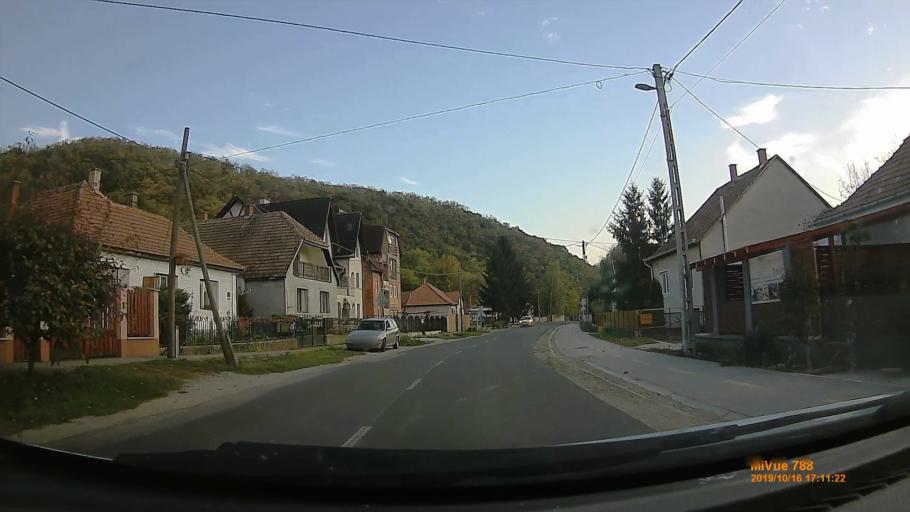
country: HU
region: Heves
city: Egerszalok
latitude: 47.8355
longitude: 20.3358
